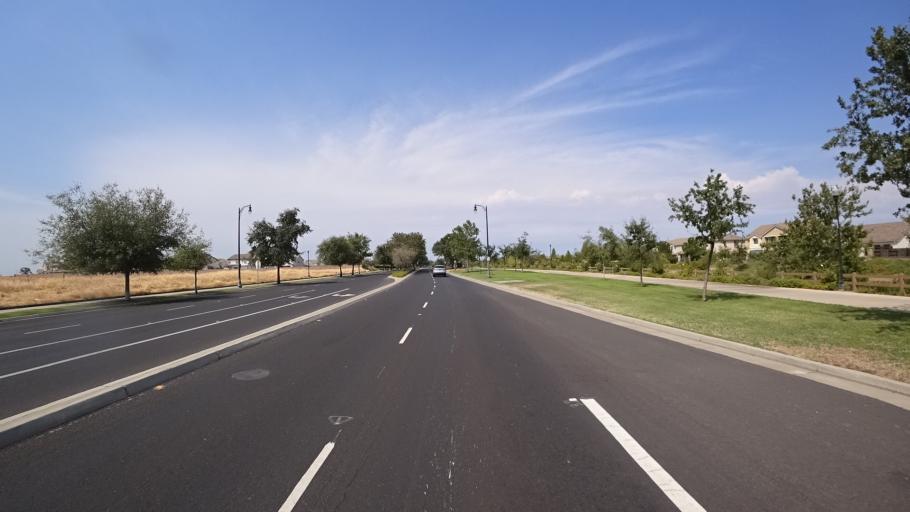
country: US
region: California
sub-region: Sacramento County
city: Elk Grove
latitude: 38.3945
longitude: -121.4002
